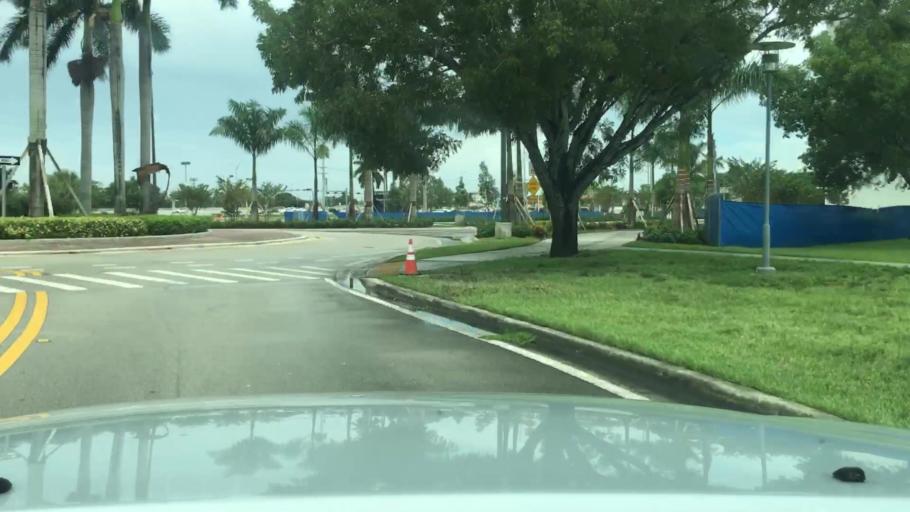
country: US
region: Florida
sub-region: Miami-Dade County
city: Sweetwater
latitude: 25.7592
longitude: -80.3703
